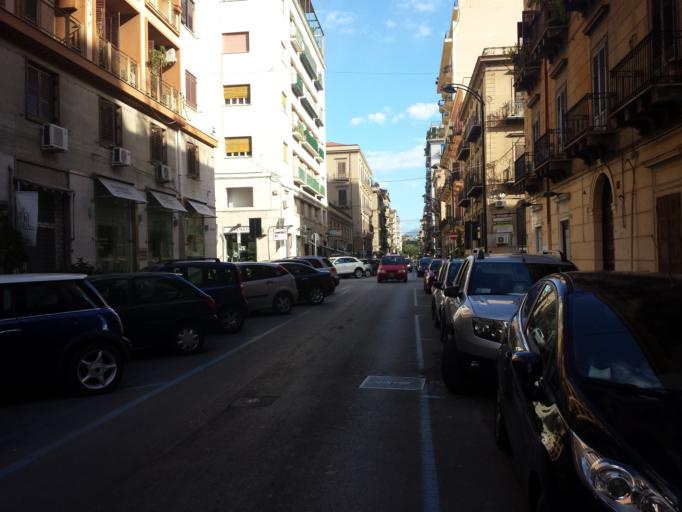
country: IT
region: Sicily
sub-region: Palermo
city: Palermo
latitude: 38.1261
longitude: 13.3558
